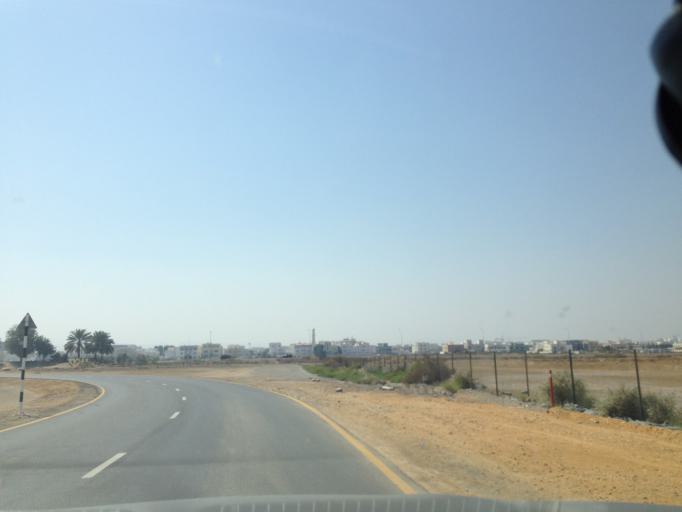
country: OM
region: Muhafazat Masqat
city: As Sib al Jadidah
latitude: 23.6294
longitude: 58.2608
